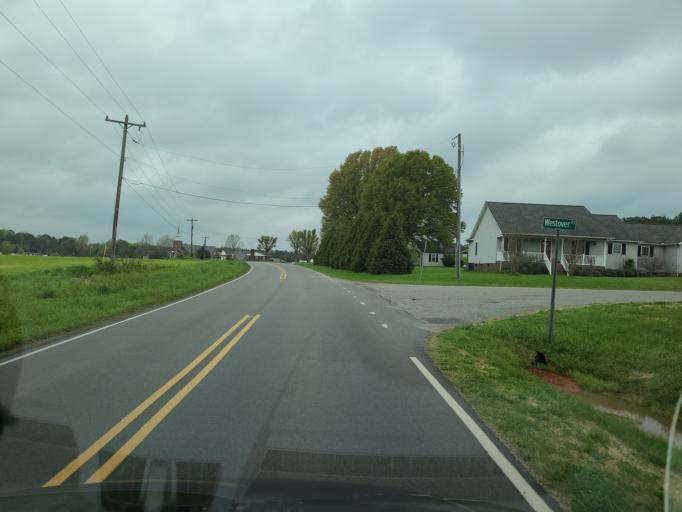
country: US
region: North Carolina
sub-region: Lincoln County
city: Lincolnton
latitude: 35.4633
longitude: -81.2948
